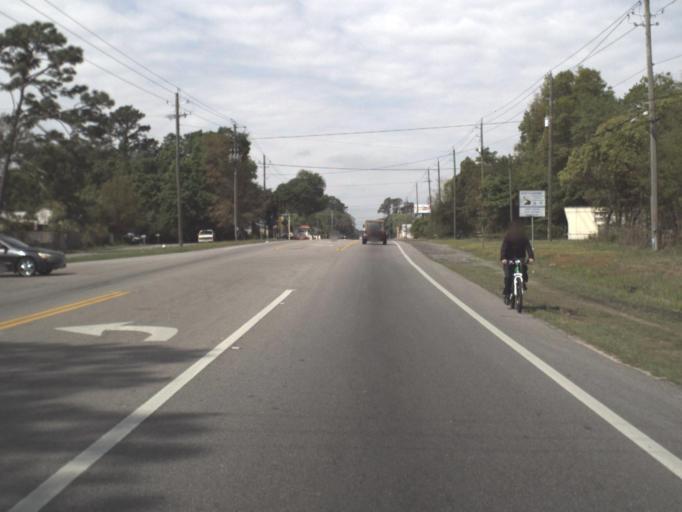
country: US
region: Florida
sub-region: Escambia County
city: Warrington
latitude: 30.3869
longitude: -87.2904
